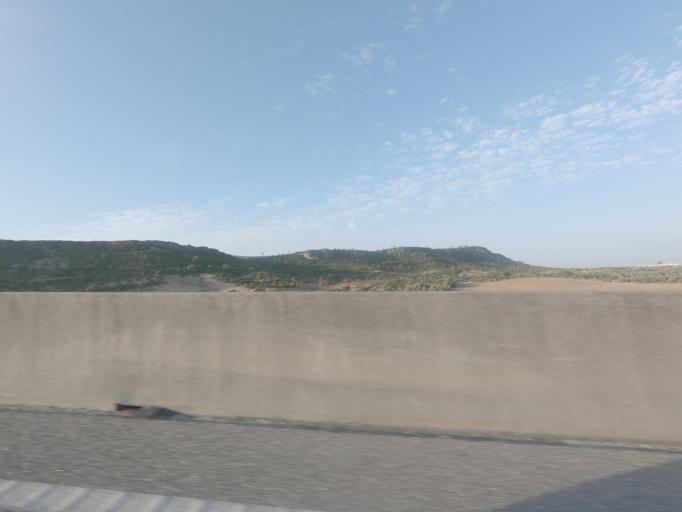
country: PT
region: Santarem
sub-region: Alcanena
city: Alcanena
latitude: 39.4868
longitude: -8.6409
